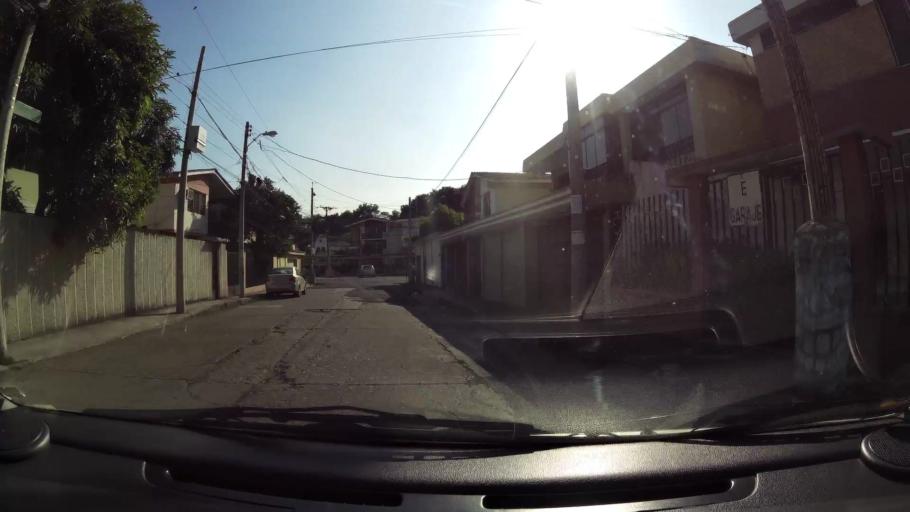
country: EC
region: Guayas
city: Guayaquil
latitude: -2.1639
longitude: -79.9031
